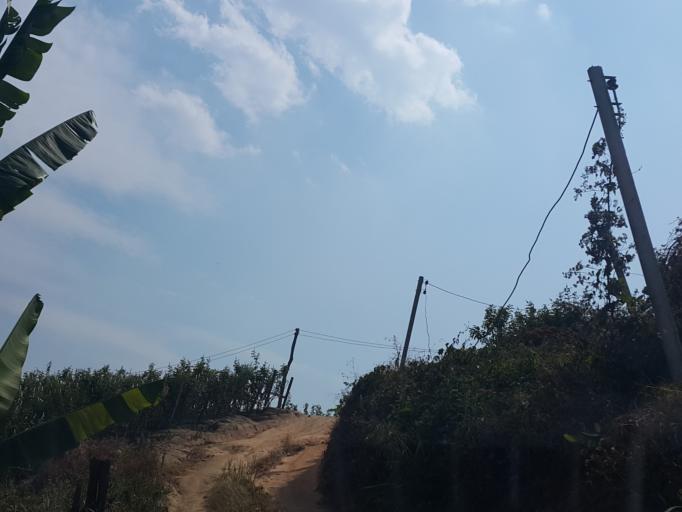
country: TH
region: Chiang Mai
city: Samoeng
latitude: 18.8841
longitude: 98.7965
